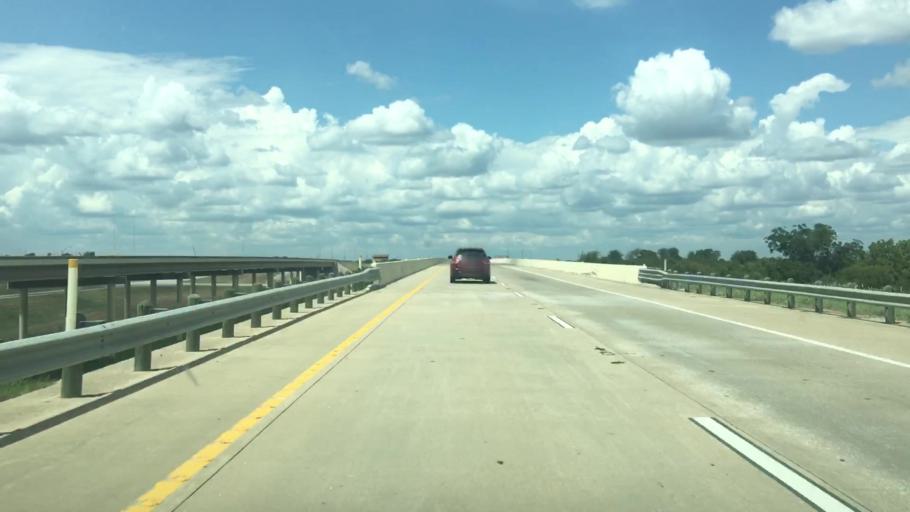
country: US
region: Texas
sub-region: Williamson County
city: Georgetown
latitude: 30.6206
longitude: -97.6133
